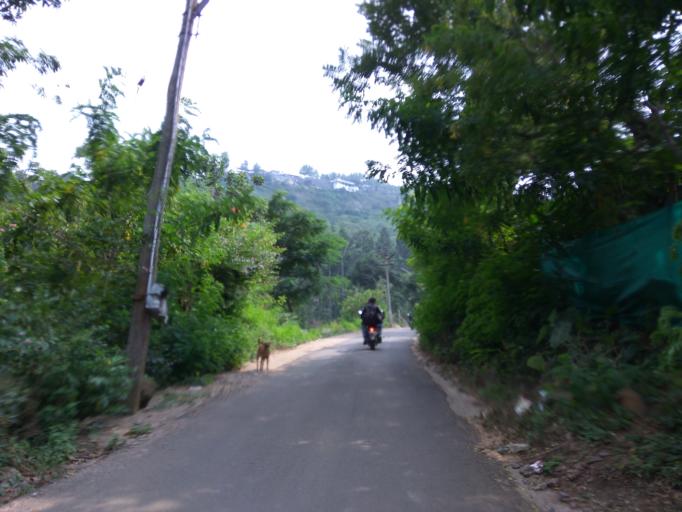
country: IN
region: Tamil Nadu
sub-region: Salem
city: Salem
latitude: 11.7898
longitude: 78.2016
